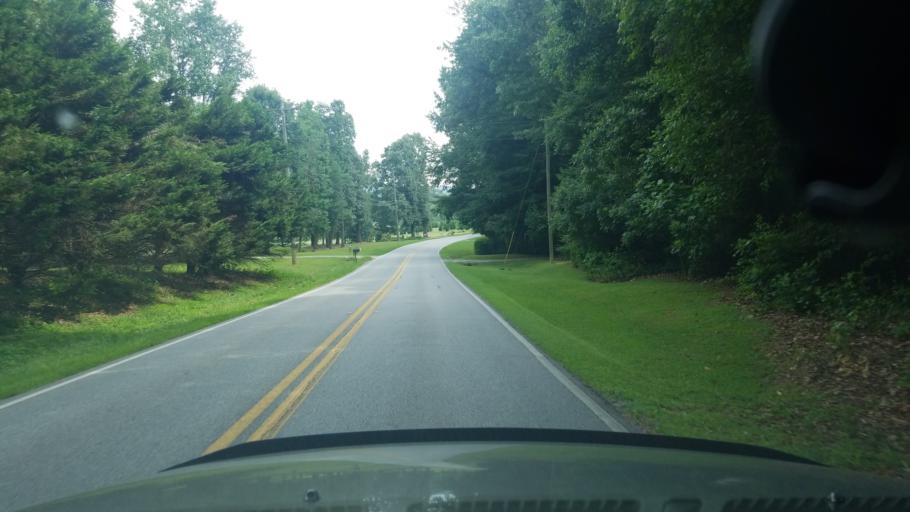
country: US
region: Georgia
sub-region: Forsyth County
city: Cumming
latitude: 34.2875
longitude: -84.1535
